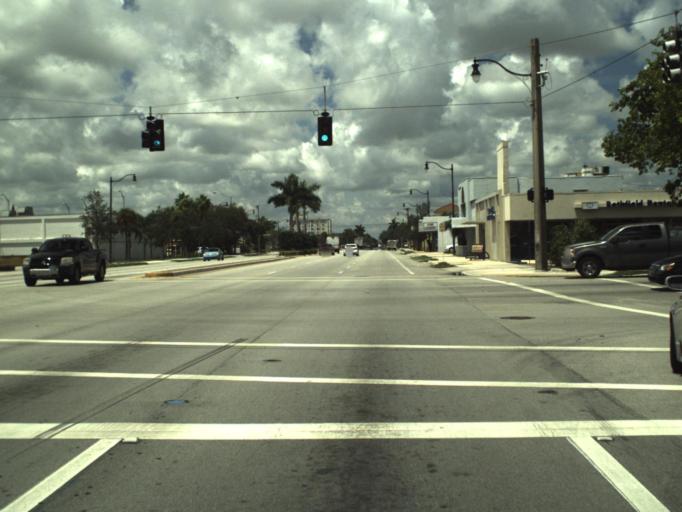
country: US
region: Florida
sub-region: Broward County
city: Carver Ranches
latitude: 26.0106
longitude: -80.1894
